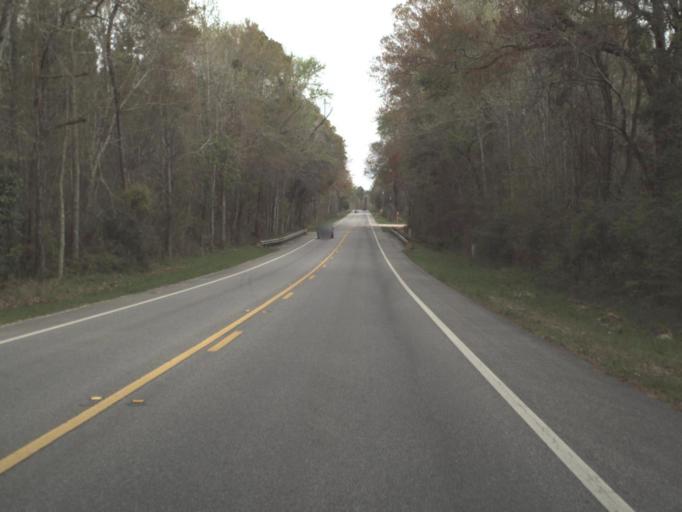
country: US
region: Florida
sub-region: Holmes County
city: Bonifay
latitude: 30.8526
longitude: -85.6666
